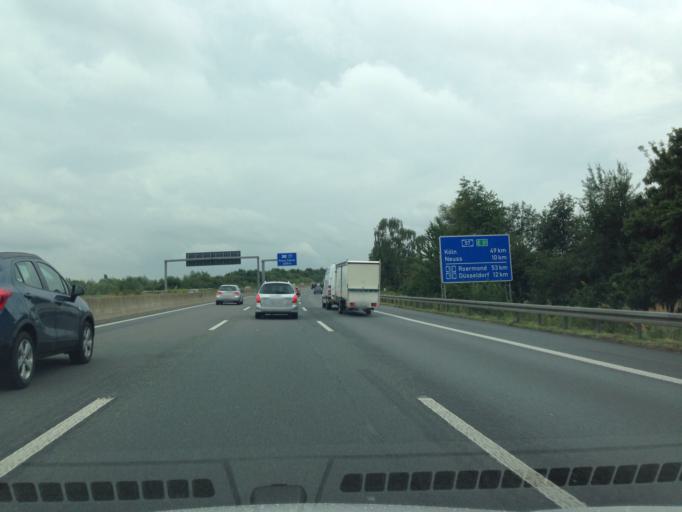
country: DE
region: North Rhine-Westphalia
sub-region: Regierungsbezirk Dusseldorf
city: Meerbusch
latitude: 51.2594
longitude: 6.6438
